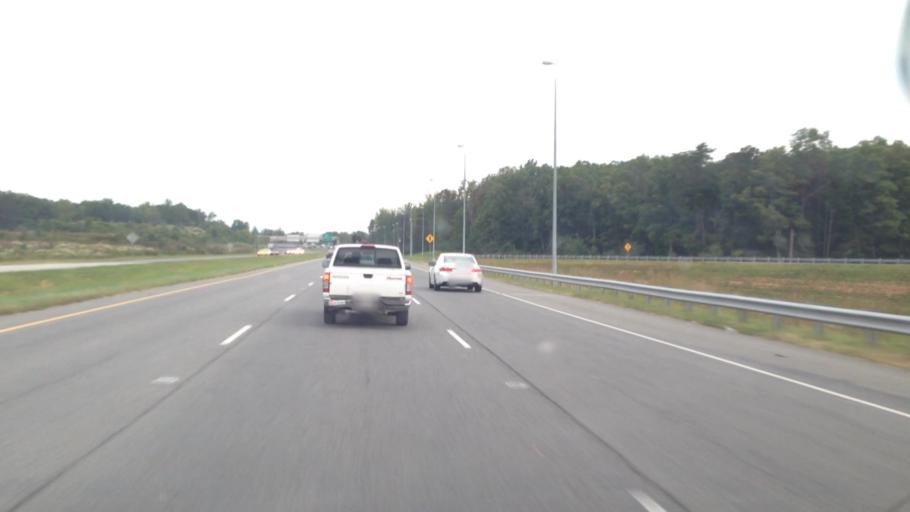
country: US
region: Virginia
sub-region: Fairfax County
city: Newington
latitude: 38.7473
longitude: -77.2090
